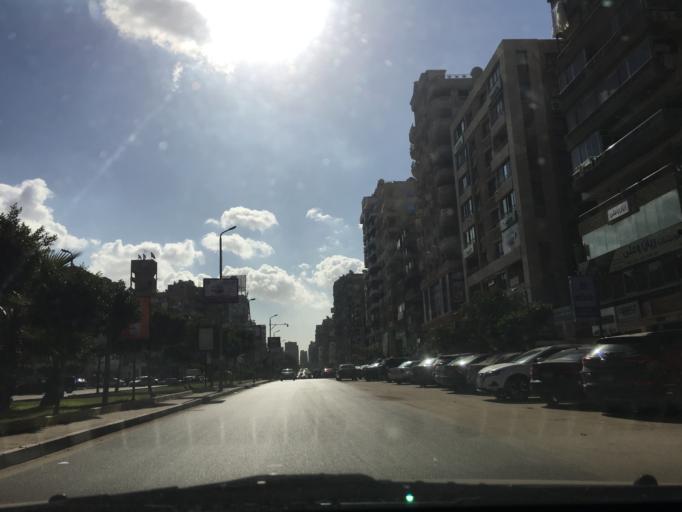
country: EG
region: Muhafazat al Qahirah
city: Cairo
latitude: 30.0575
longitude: 31.3457
